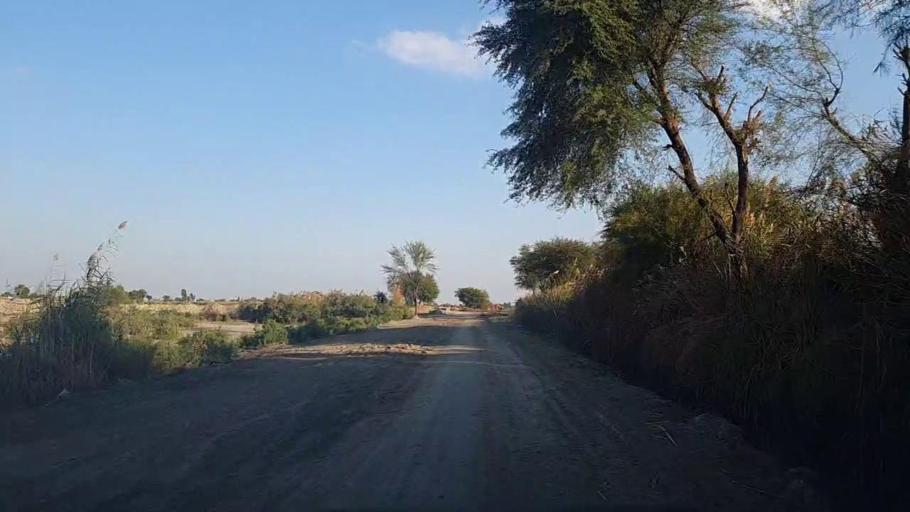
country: PK
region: Sindh
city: Jhol
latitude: 25.9199
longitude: 69.0397
